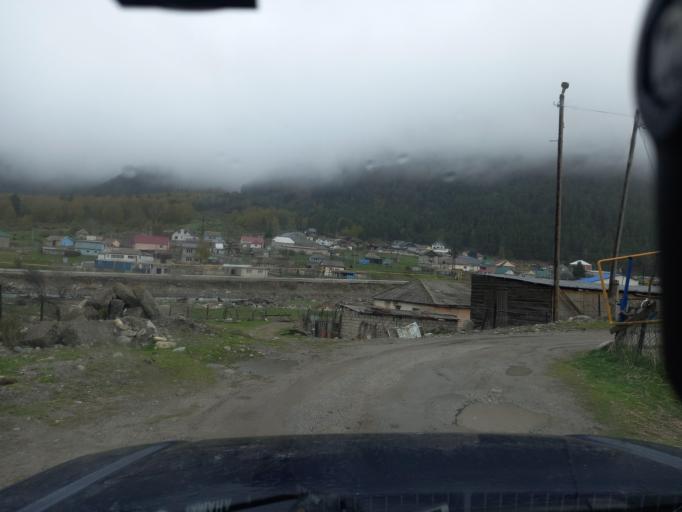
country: RU
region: Kabardino-Balkariya
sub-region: El'brusskiy Rayon
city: El'brus
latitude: 43.2617
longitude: 42.6499
